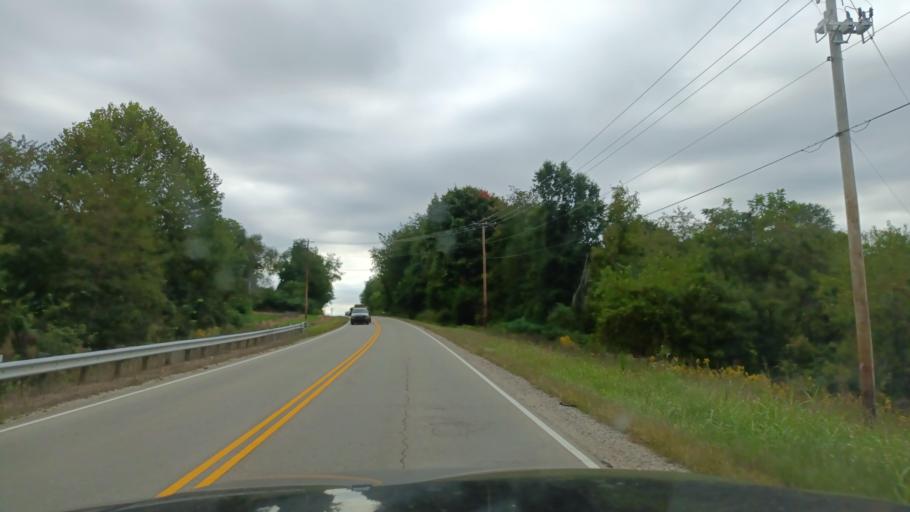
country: US
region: Ohio
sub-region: Ross County
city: Chillicothe
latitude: 39.2820
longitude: -82.8426
